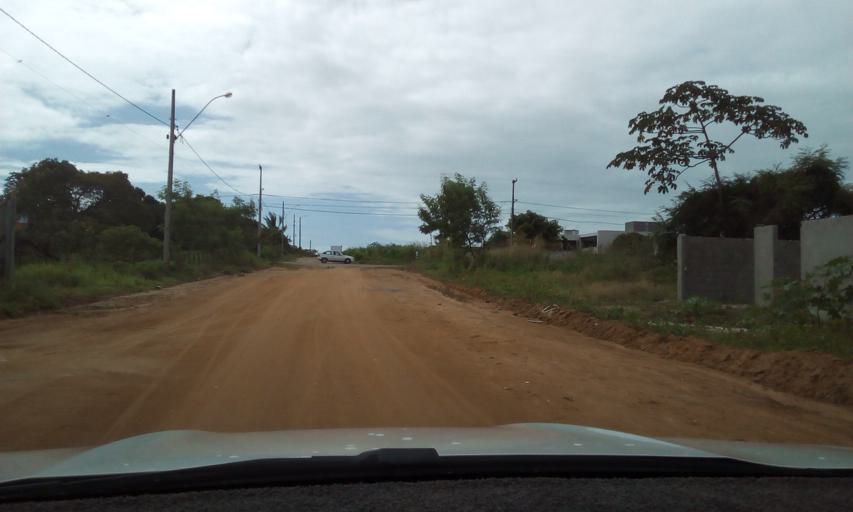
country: BR
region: Paraiba
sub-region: Joao Pessoa
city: Joao Pessoa
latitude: -7.1482
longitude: -34.8132
